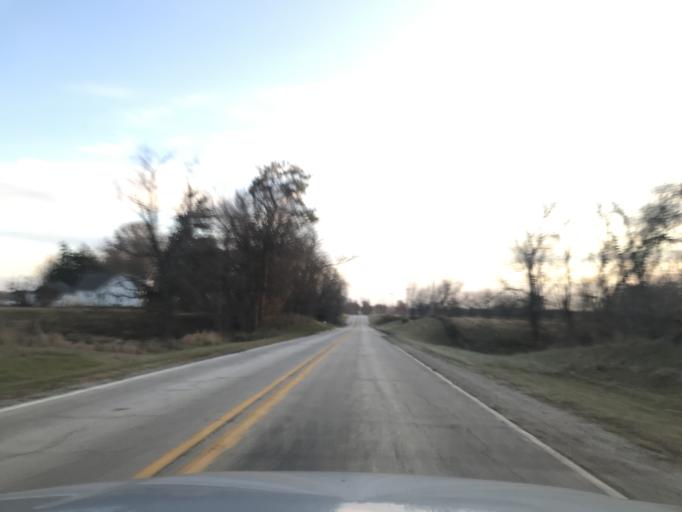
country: US
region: Illinois
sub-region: Henderson County
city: Oquawka
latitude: 40.9352
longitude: -90.8641
